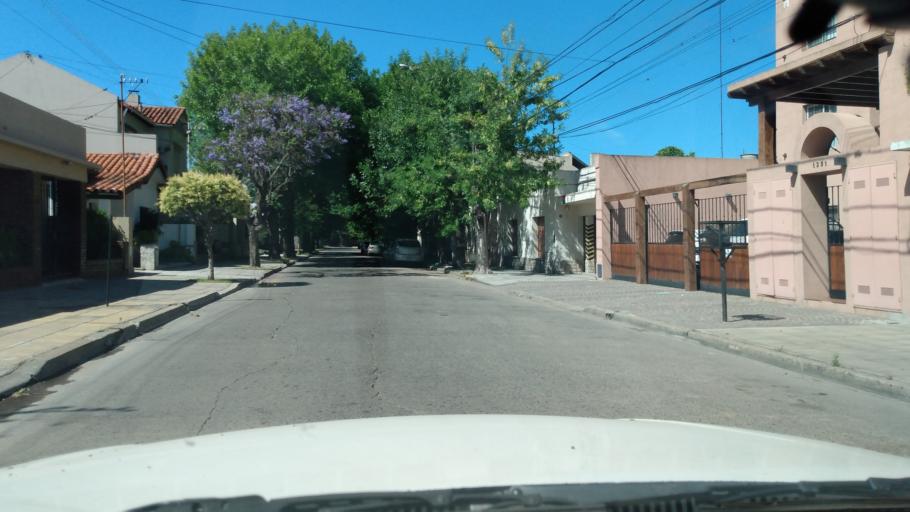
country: AR
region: Buenos Aires
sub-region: Partido de Lujan
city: Lujan
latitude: -34.5711
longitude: -59.1113
